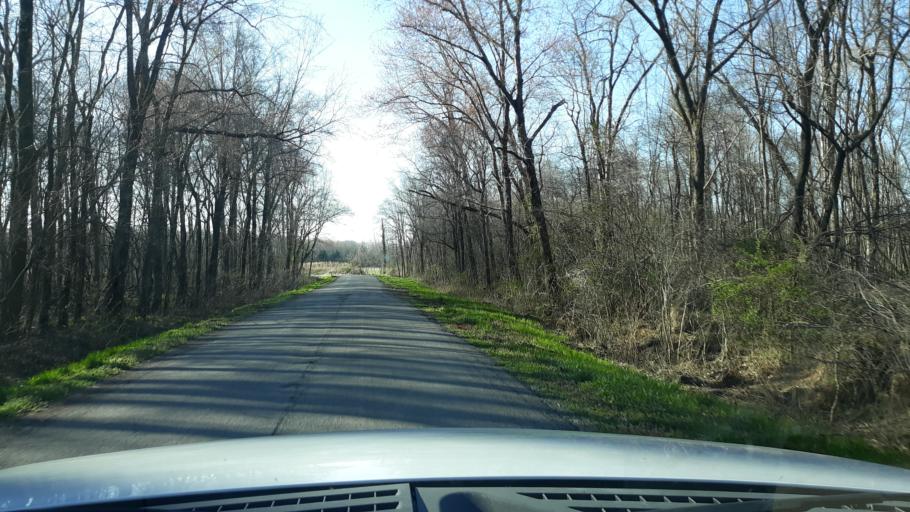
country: US
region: Illinois
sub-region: Saline County
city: Harrisburg
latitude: 37.7618
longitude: -88.5709
